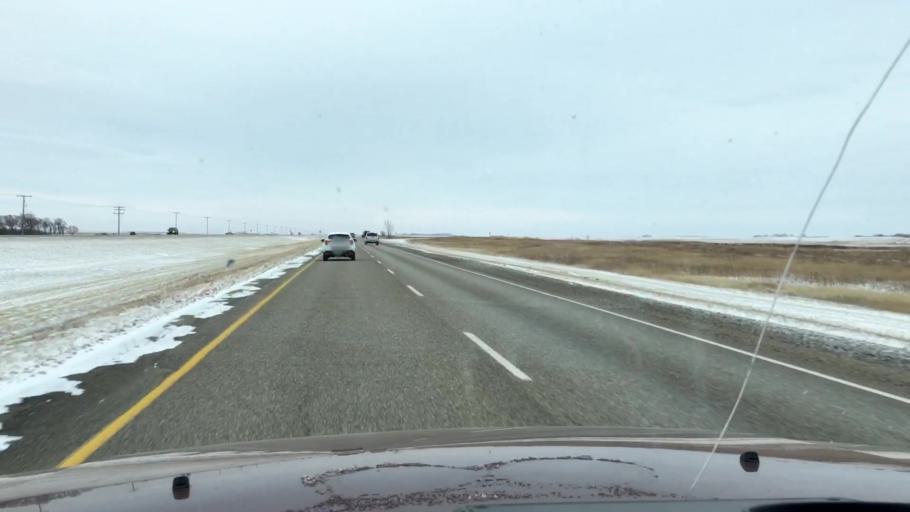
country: CA
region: Saskatchewan
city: Moose Jaw
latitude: 51.0111
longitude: -105.7760
